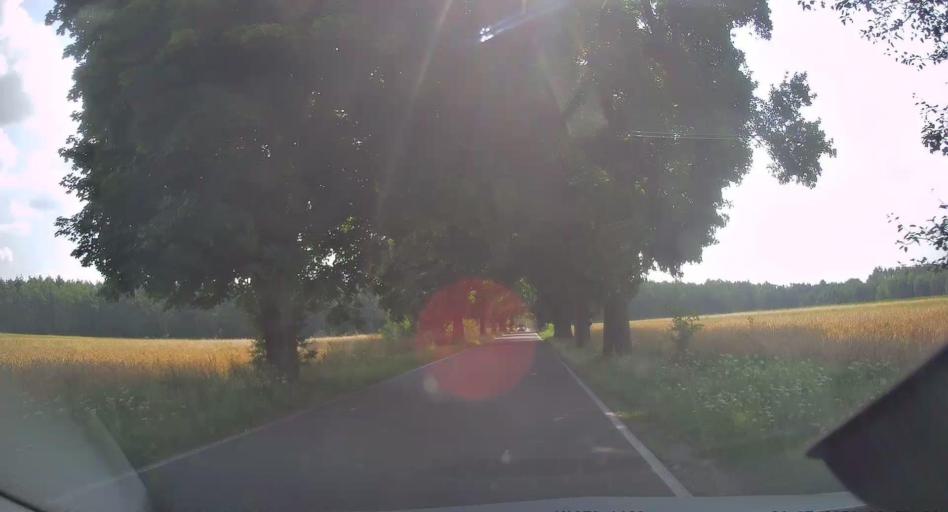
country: PL
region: Lodz Voivodeship
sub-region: Powiat tomaszowski
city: Lubochnia
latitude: 51.5624
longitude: 20.1229
